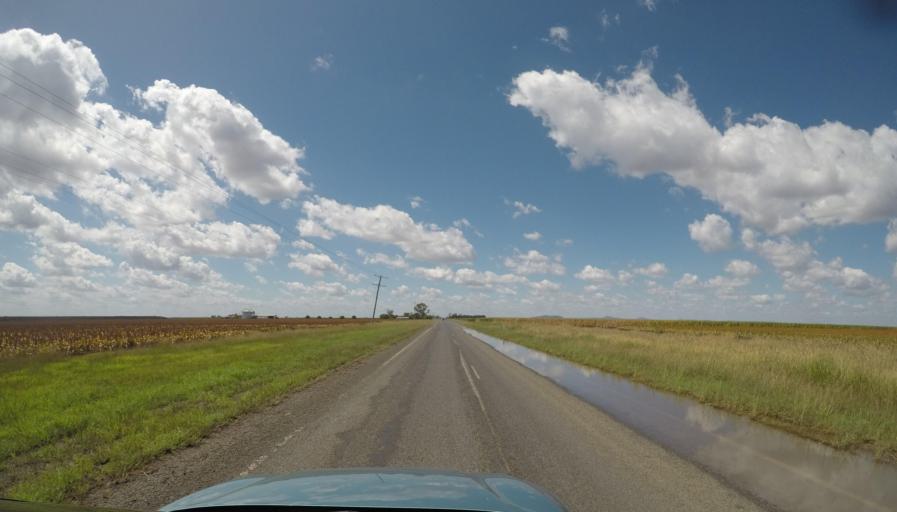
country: AU
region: Queensland
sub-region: Toowoomba
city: Oakey
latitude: -27.5181
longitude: 151.4140
